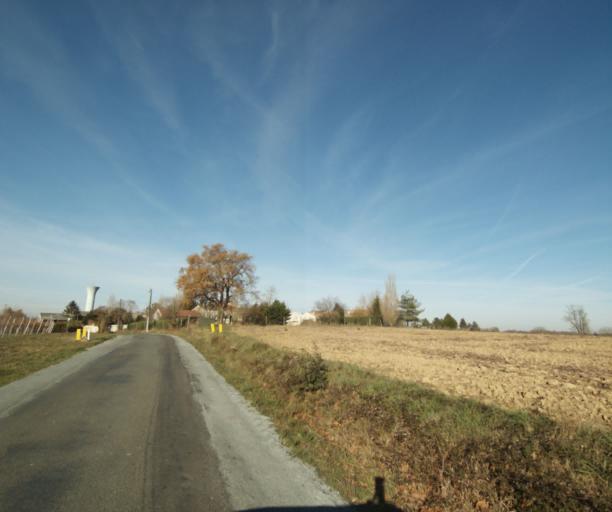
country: FR
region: Poitou-Charentes
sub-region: Departement de la Charente-Maritime
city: Chaniers
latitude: 45.7388
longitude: -0.5675
